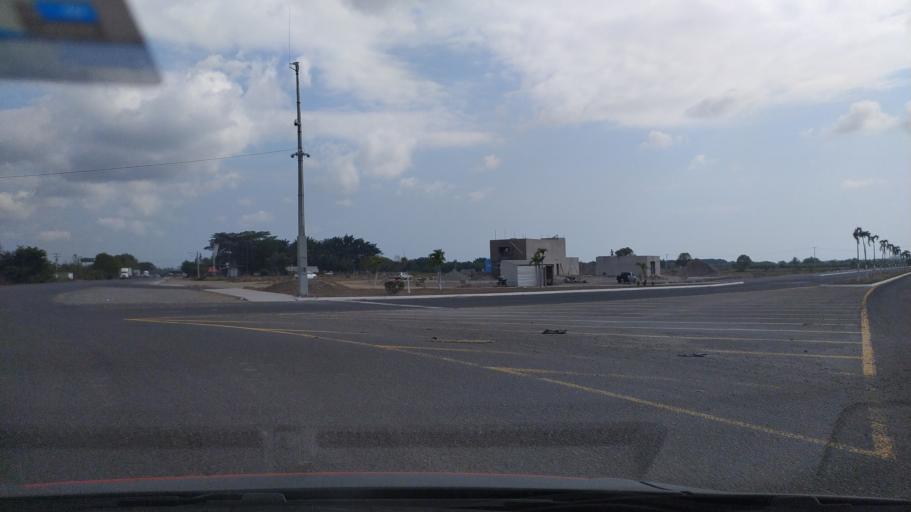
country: MX
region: Colima
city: Tecoman
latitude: 18.8970
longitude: -103.8599
